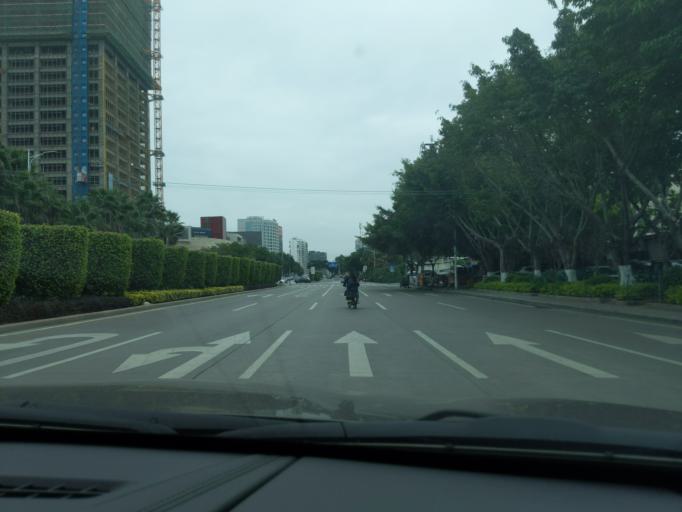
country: CN
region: Fujian
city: Liuwudian
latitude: 24.4877
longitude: 118.1638
